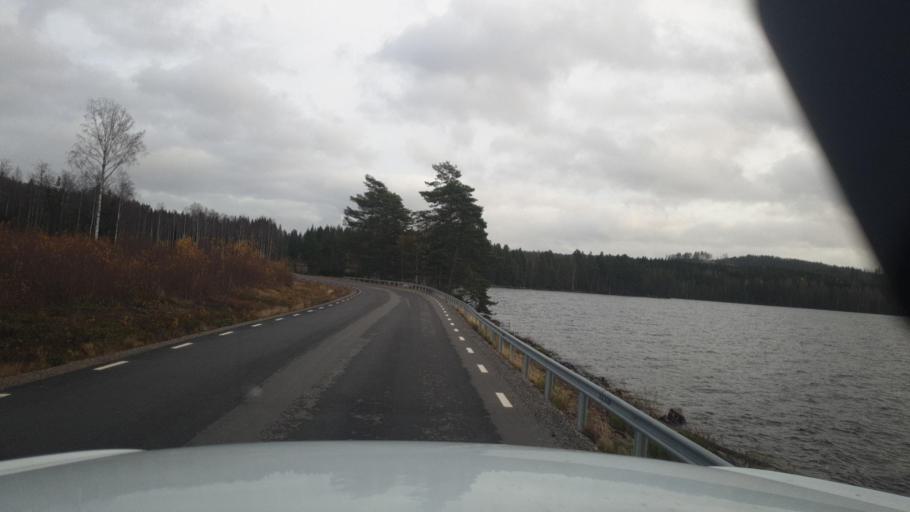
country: SE
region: Vaermland
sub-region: Torsby Kommun
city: Torsby
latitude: 59.9805
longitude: 12.7969
